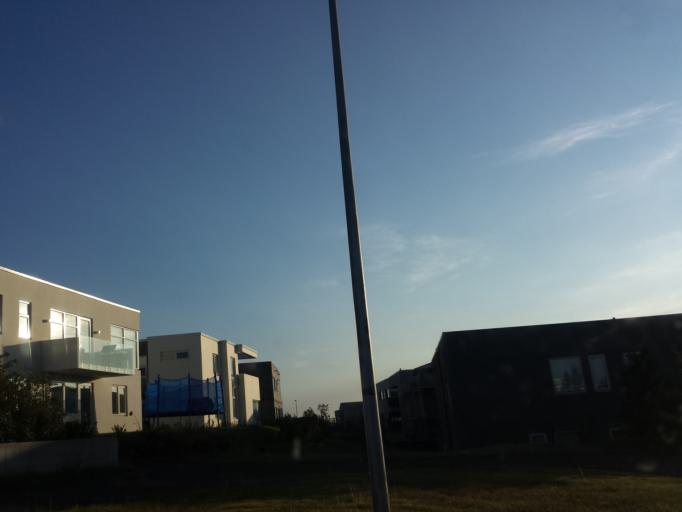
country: IS
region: Capital Region
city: Kopavogur
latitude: 64.0882
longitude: -21.8598
